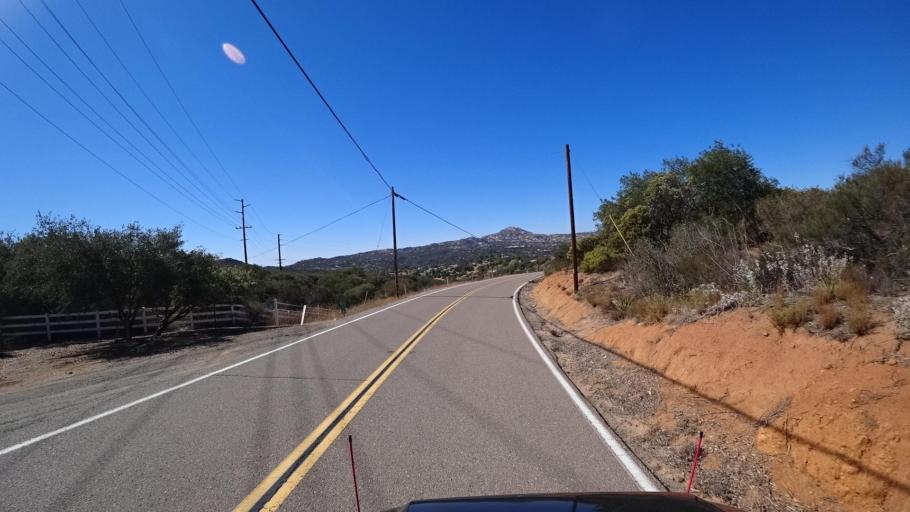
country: US
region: California
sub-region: San Diego County
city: Descanso
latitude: 32.7757
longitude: -116.6680
